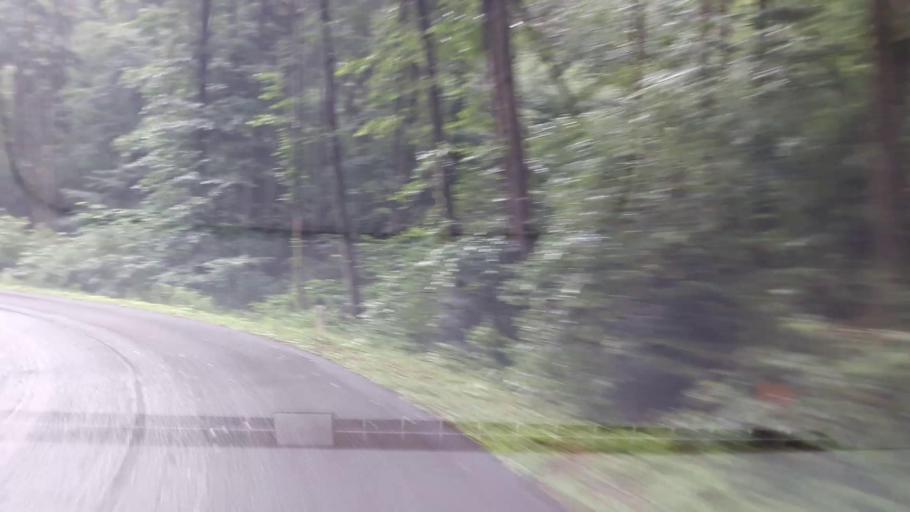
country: AT
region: Lower Austria
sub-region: Politischer Bezirk Krems
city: Aggsbach
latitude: 48.2887
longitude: 15.3900
